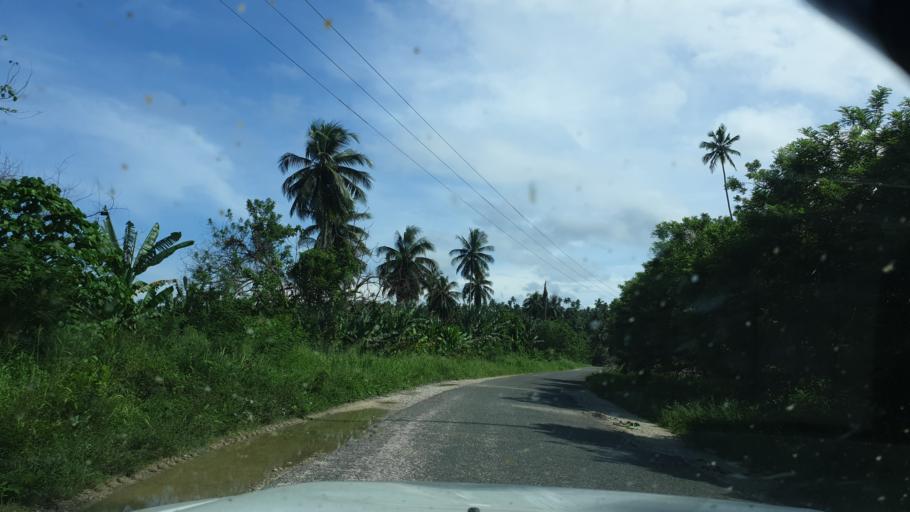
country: PG
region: Madang
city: Madang
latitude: -4.7993
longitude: 145.7310
